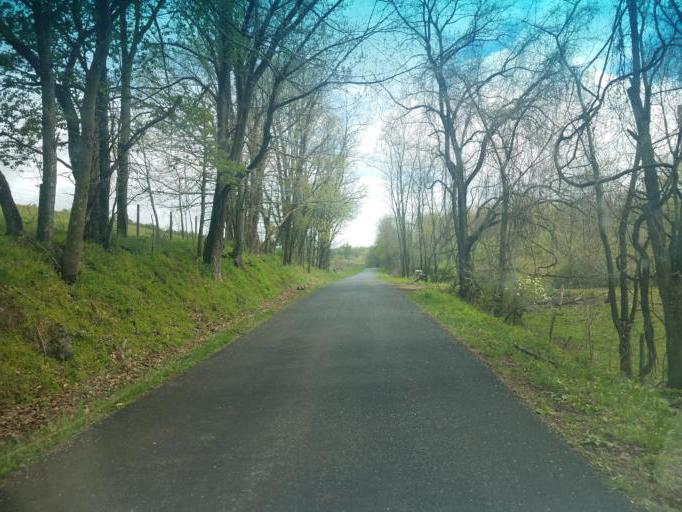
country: US
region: Virginia
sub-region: Smyth County
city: Atkins
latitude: 36.9485
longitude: -81.4128
